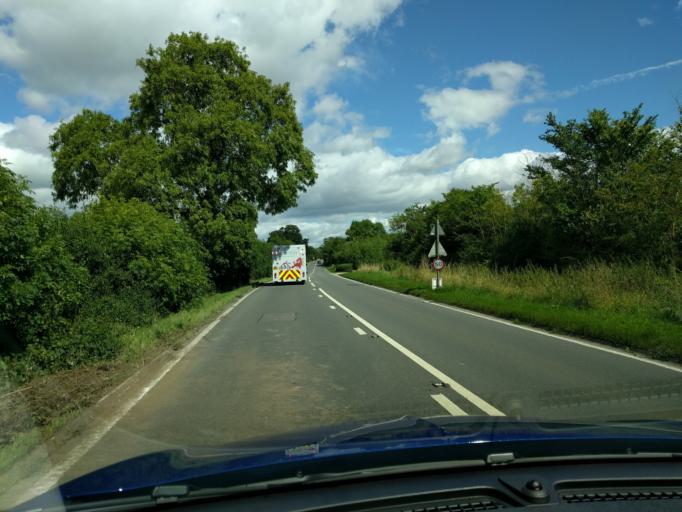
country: GB
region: England
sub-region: Warwickshire
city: Stratford-upon-Avon
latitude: 52.1591
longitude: -1.7296
